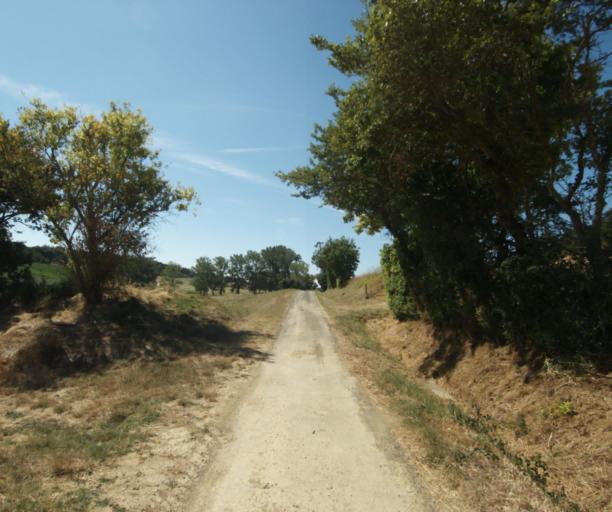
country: FR
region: Midi-Pyrenees
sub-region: Departement de la Haute-Garonne
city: Saint-Felix-Lauragais
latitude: 43.4991
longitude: 1.9321
